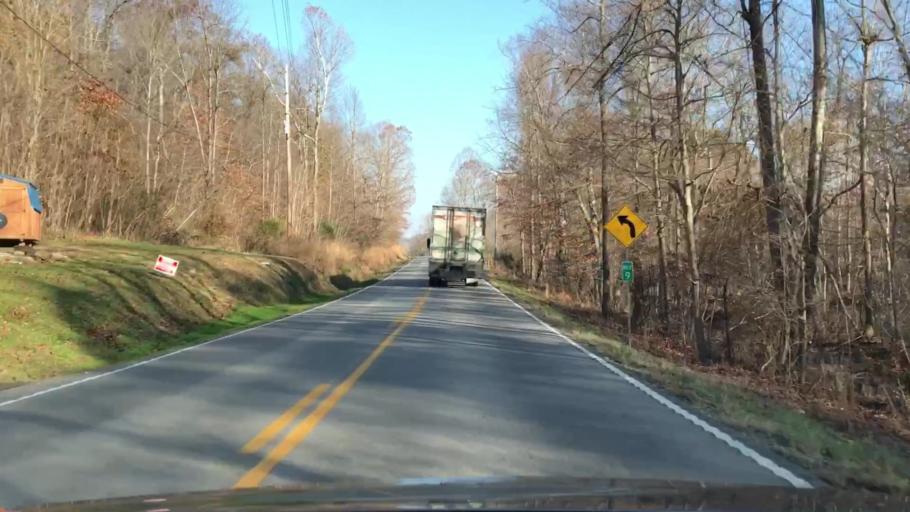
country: US
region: Kentucky
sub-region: Grayson County
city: Leitchfield
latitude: 37.4224
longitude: -86.2785
